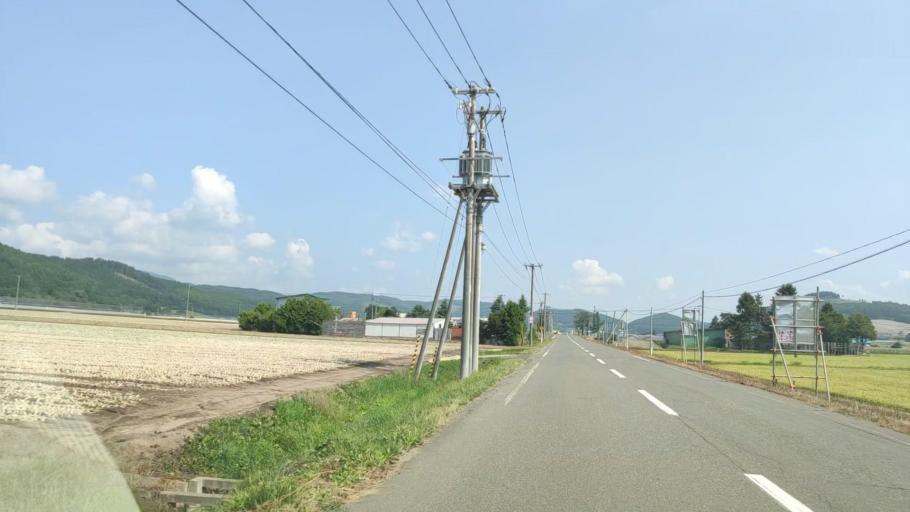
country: JP
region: Hokkaido
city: Shimo-furano
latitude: 43.3889
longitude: 142.3940
